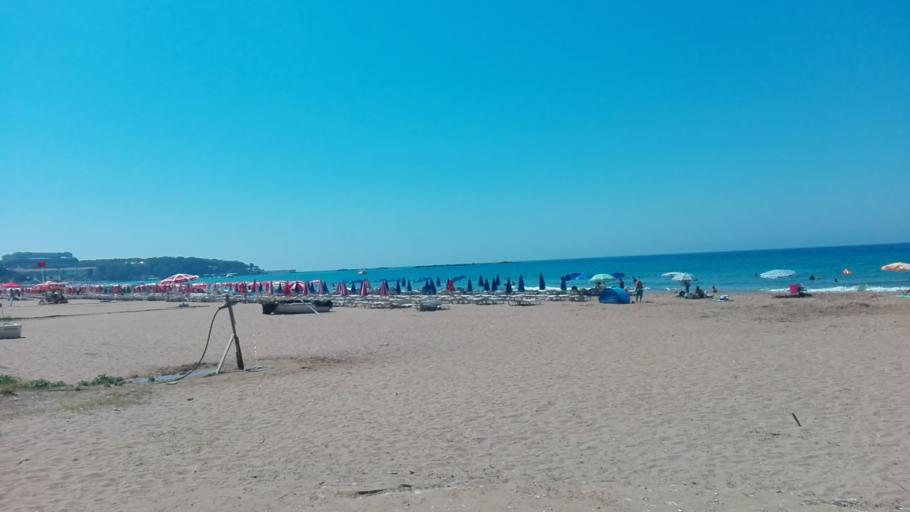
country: TR
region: Antalya
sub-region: Alanya
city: Avsallar
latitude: 36.6385
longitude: 31.7449
